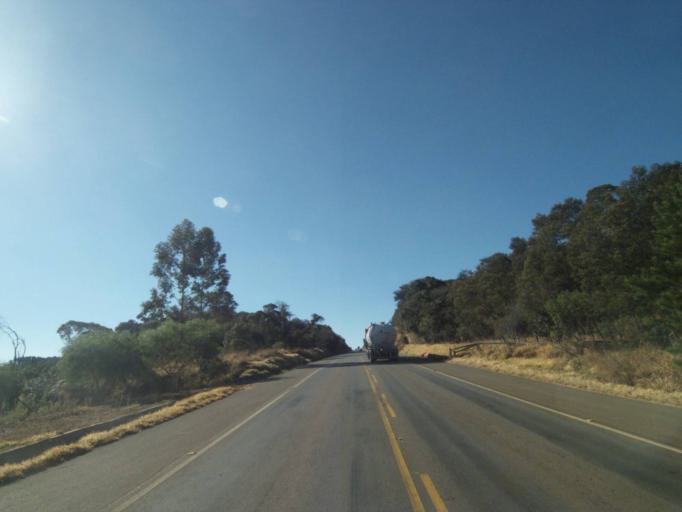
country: BR
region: Parana
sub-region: Tibagi
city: Tibagi
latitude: -24.6084
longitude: -50.4424
